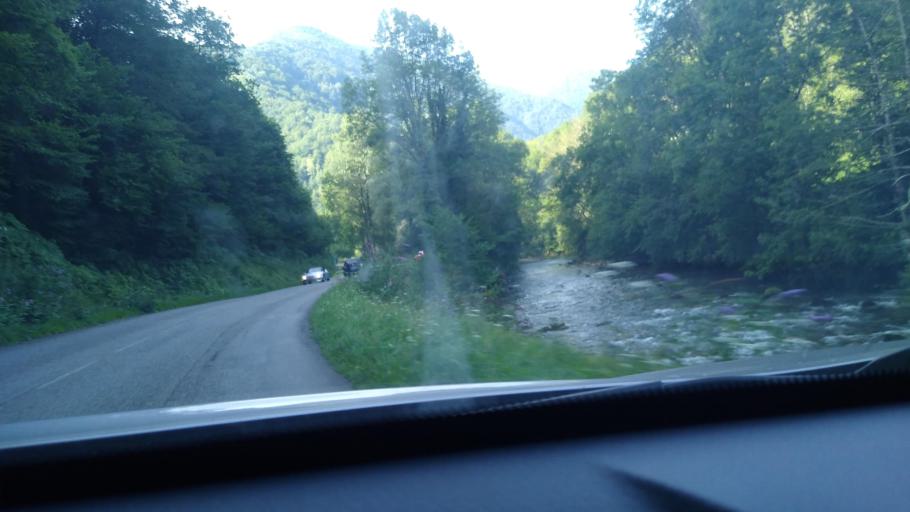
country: FR
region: Midi-Pyrenees
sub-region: Departement de l'Ariege
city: Saint-Girons
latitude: 42.8470
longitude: 1.1927
